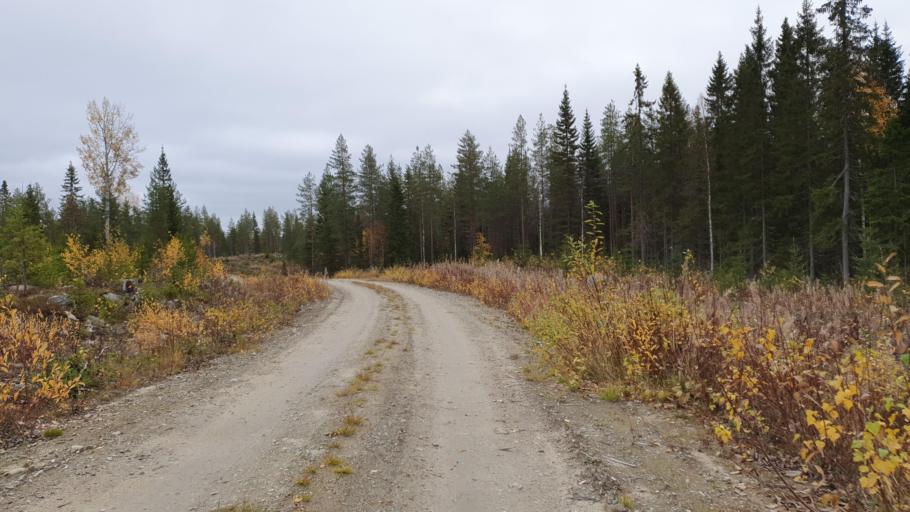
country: FI
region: Kainuu
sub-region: Kehys-Kainuu
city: Kuhmo
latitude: 64.4438
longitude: 29.6463
